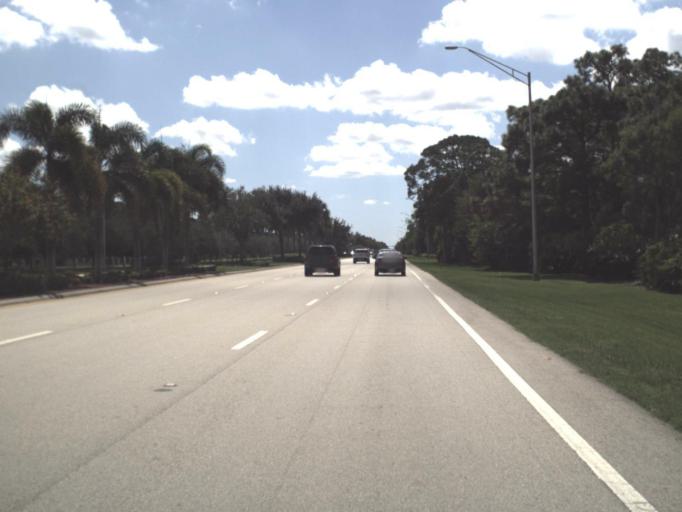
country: US
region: Florida
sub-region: Collier County
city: Pine Ridge
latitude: 26.2267
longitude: -81.8009
